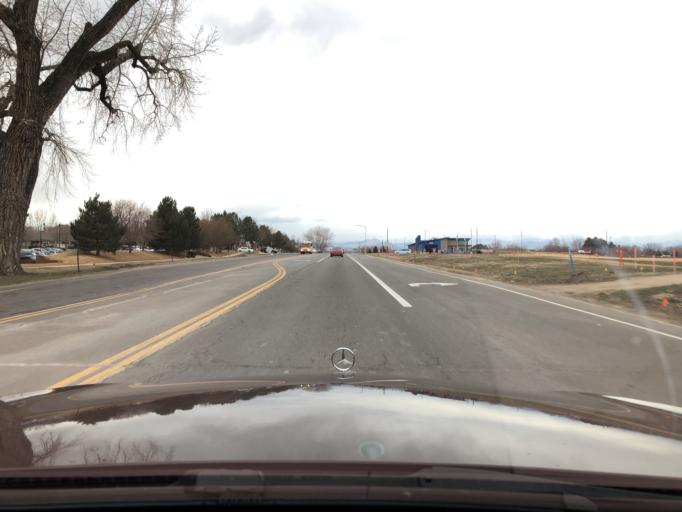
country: US
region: Colorado
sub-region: Boulder County
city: Louisville
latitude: 40.0147
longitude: -105.1258
